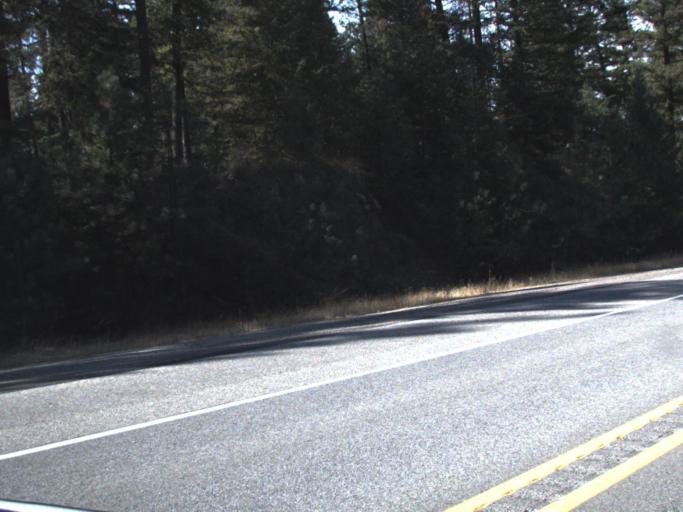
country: US
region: Washington
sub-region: Spokane County
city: Deer Park
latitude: 47.9277
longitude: -117.3514
